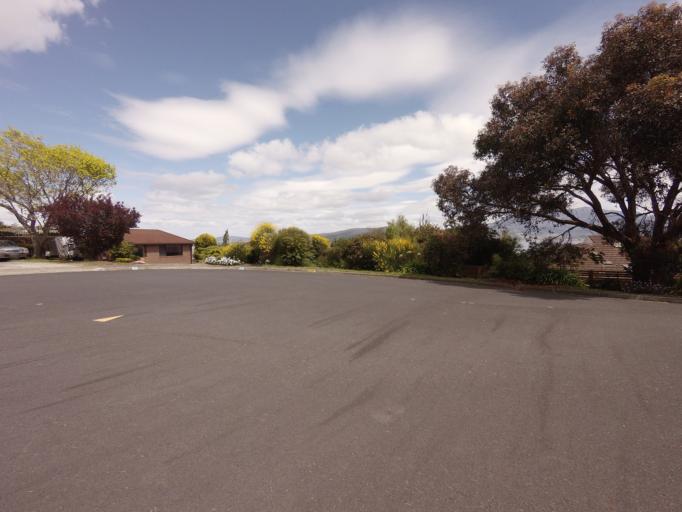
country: AU
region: Tasmania
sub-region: Clarence
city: Howrah
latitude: -42.8890
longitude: 147.4125
